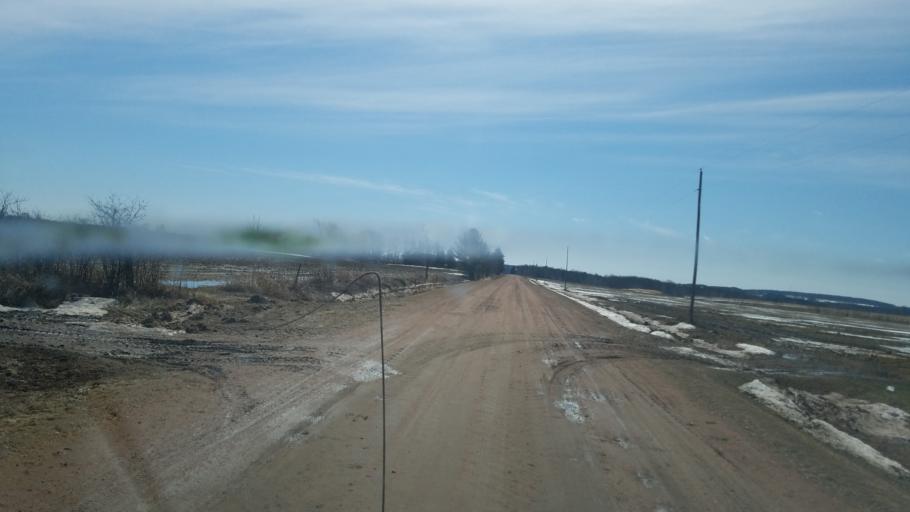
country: US
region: Wisconsin
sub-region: Clark County
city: Loyal
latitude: 44.6148
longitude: -90.4273
